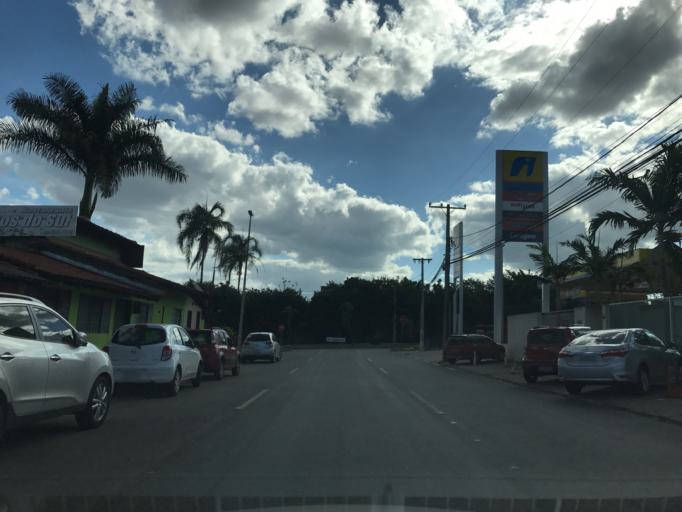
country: BR
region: Federal District
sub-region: Brasilia
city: Brasilia
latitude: -15.8021
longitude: -47.9706
